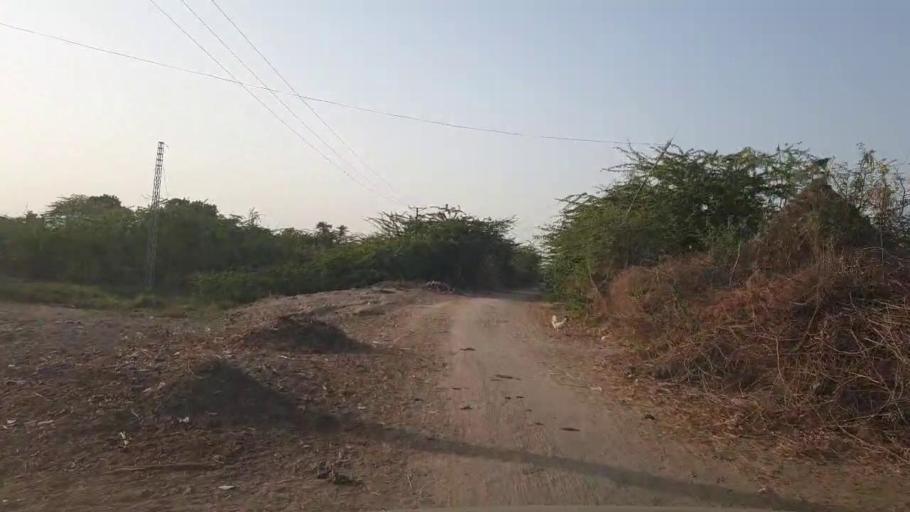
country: PK
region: Sindh
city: Dhoro Naro
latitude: 25.4987
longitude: 69.5591
